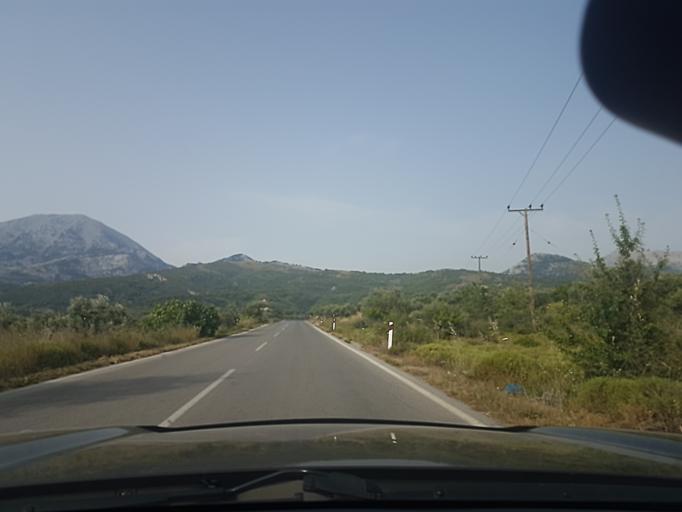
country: GR
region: Central Greece
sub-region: Nomos Evvoias
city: Yimnon
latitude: 38.5739
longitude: 23.8030
